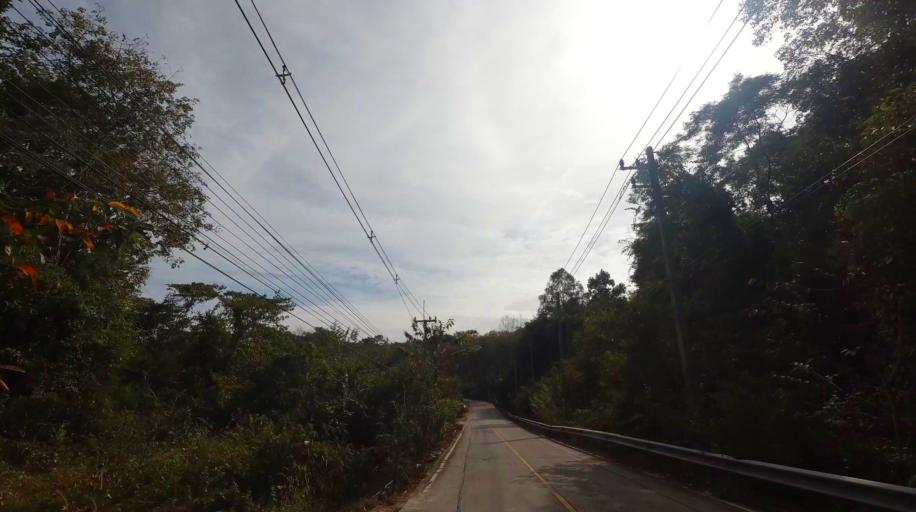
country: TH
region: Trat
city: Ko Kut
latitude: 11.6116
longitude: 102.5421
